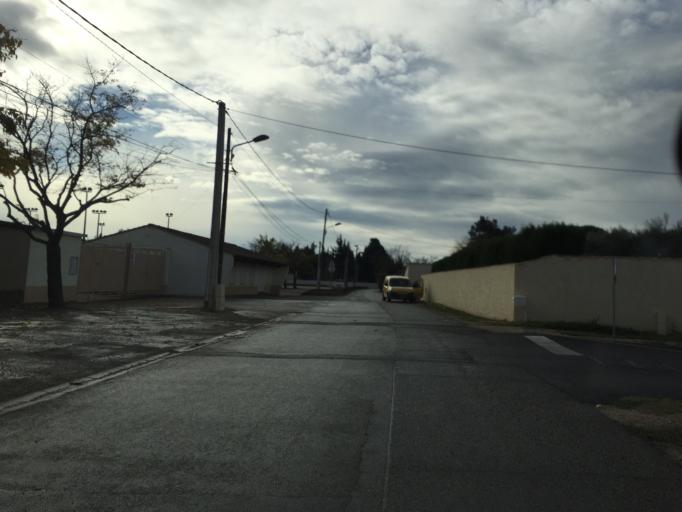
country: FR
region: Provence-Alpes-Cote d'Azur
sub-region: Departement du Vaucluse
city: Vedene
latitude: 43.9944
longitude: 4.8901
